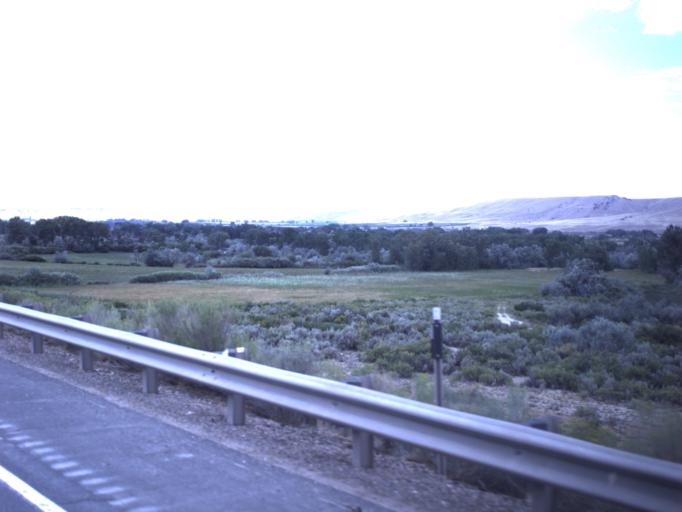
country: US
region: Utah
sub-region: Duchesne County
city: Duchesne
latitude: 40.1588
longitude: -110.2633
